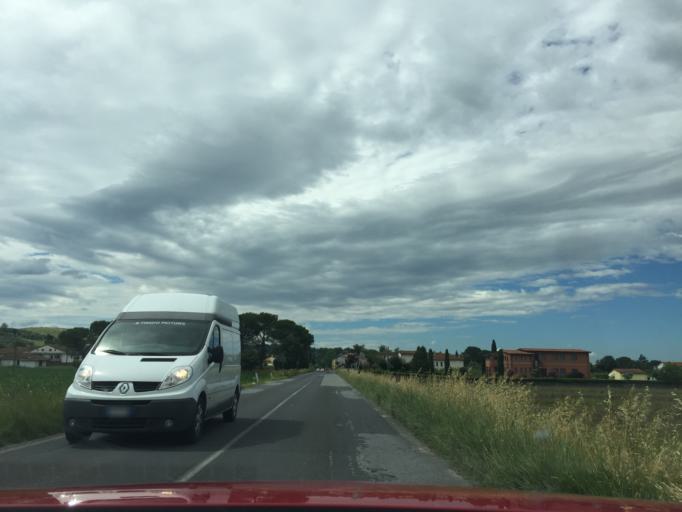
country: IT
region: Tuscany
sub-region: Province of Florence
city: Fucecchio
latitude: 43.7488
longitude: 10.8202
